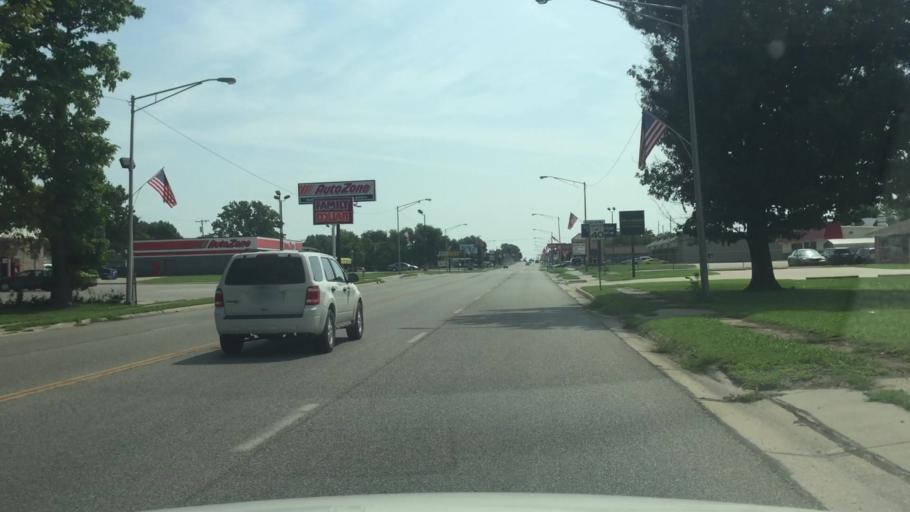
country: US
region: Kansas
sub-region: Montgomery County
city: Coffeyville
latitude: 37.0330
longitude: -95.6316
